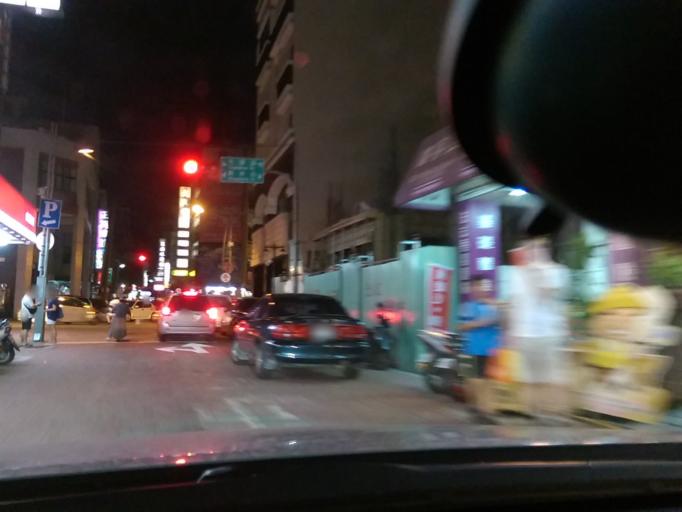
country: TW
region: Taiwan
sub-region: Chiayi
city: Jiayi Shi
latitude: 23.4790
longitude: 120.4508
